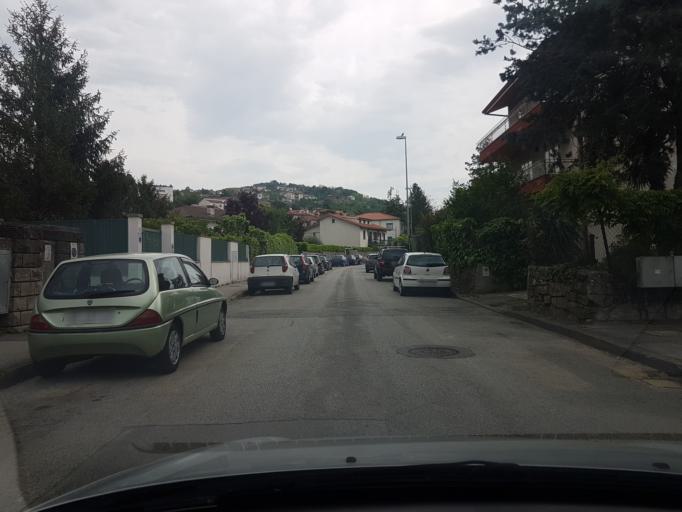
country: IT
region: Friuli Venezia Giulia
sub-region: Provincia di Trieste
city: Muggia
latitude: 45.6014
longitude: 13.7676
